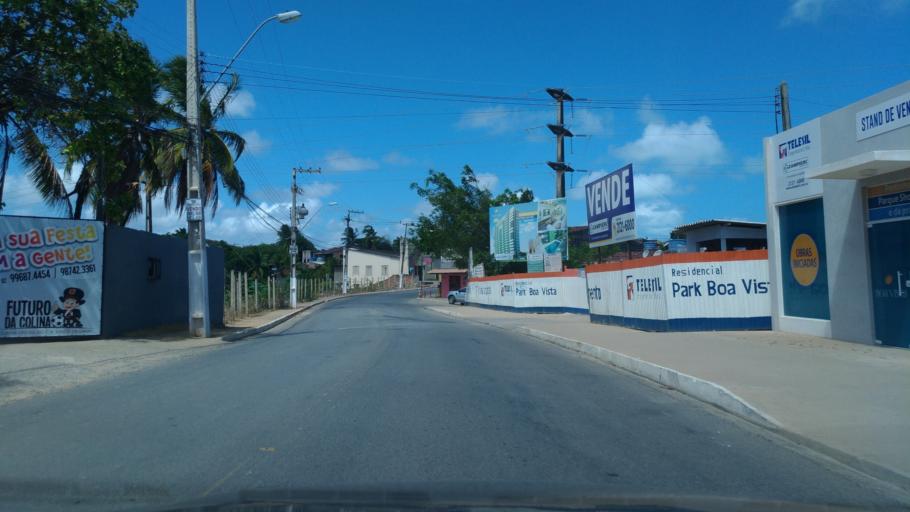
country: BR
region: Alagoas
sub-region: Maceio
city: Maceio
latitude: -9.6192
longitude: -35.7070
